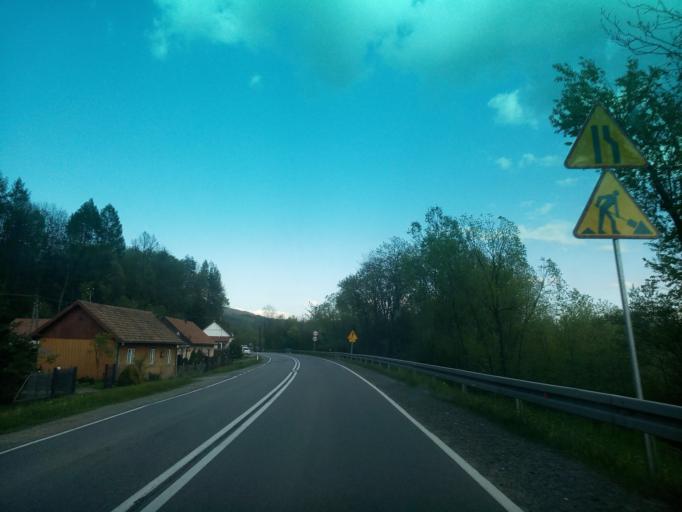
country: PL
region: Lesser Poland Voivodeship
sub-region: Powiat nowosadecki
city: Labowa
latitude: 49.5325
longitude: 20.8296
